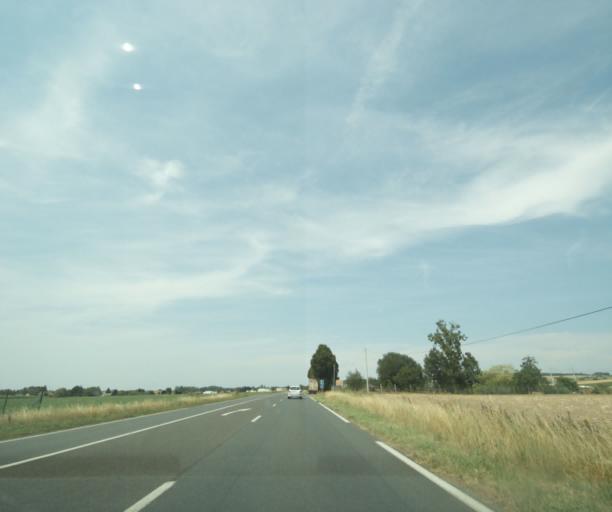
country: FR
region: Poitou-Charentes
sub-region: Departement de la Vienne
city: Dange-Saint-Romain
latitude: 46.9515
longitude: 0.6075
